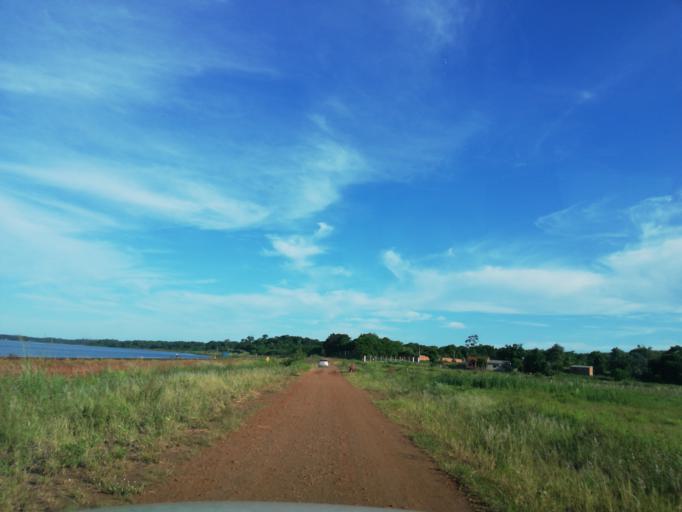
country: AR
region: Misiones
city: Garupa
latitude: -27.4503
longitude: -55.8363
